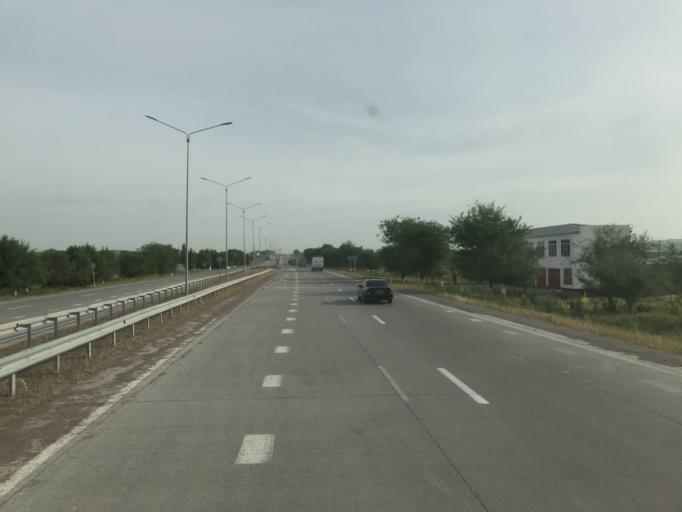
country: KZ
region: Ongtustik Qazaqstan
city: Qazyqurt
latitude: 41.7966
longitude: 69.3934
